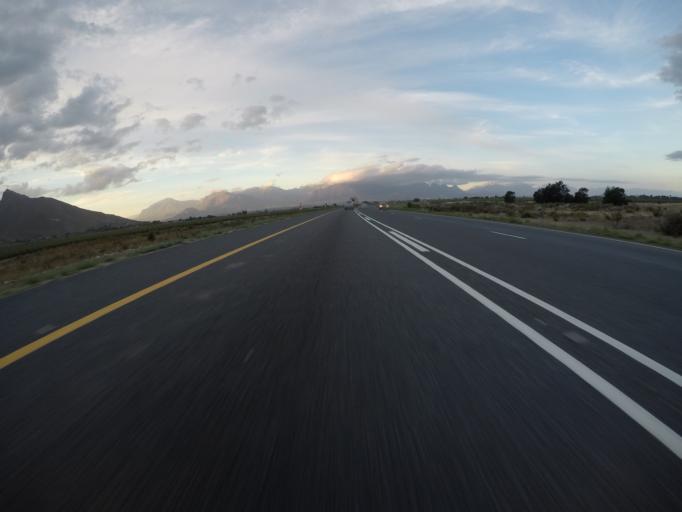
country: ZA
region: Western Cape
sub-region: Cape Winelands District Municipality
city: Worcester
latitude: -33.6898
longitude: 19.2691
